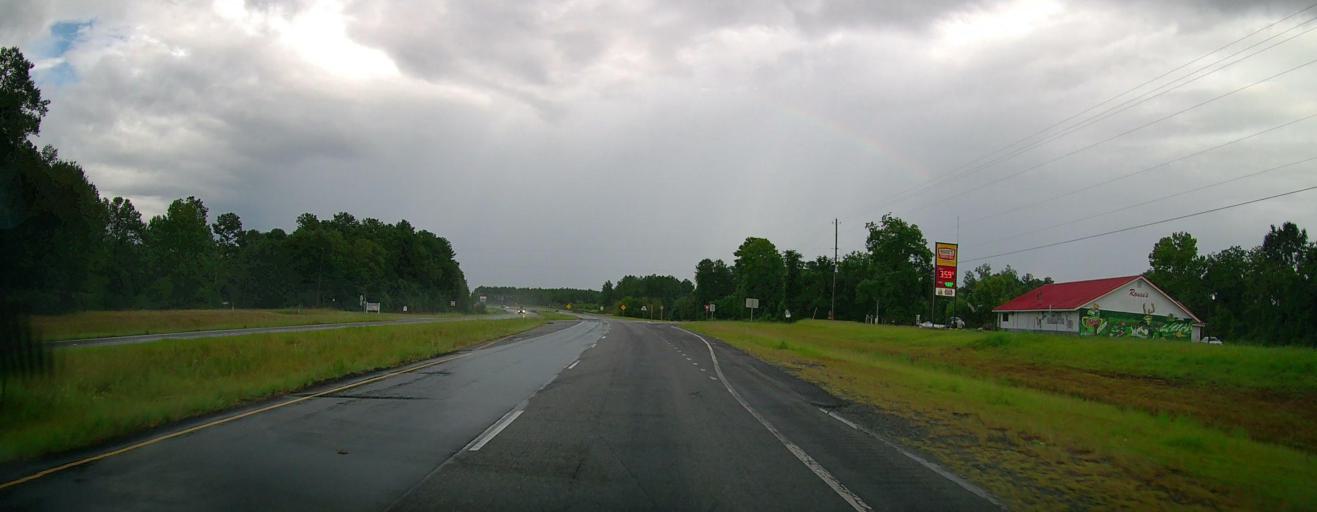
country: US
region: Georgia
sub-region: Ware County
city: Deenwood
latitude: 31.2542
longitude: -82.4798
